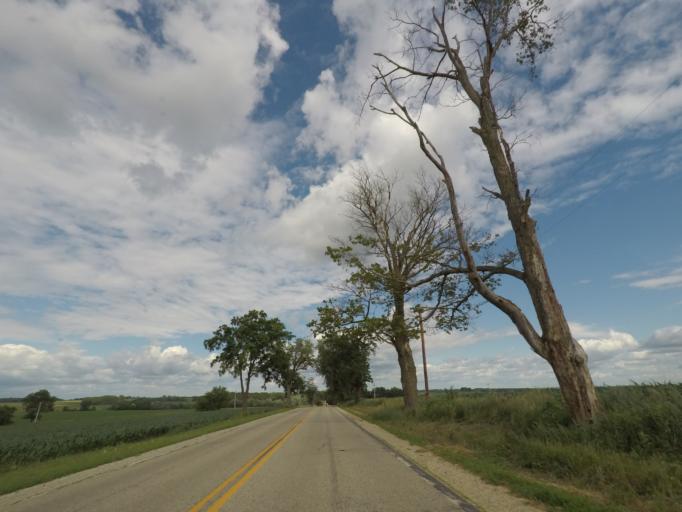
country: US
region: Wisconsin
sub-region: Rock County
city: Orfordville
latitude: 42.7115
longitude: -89.2027
